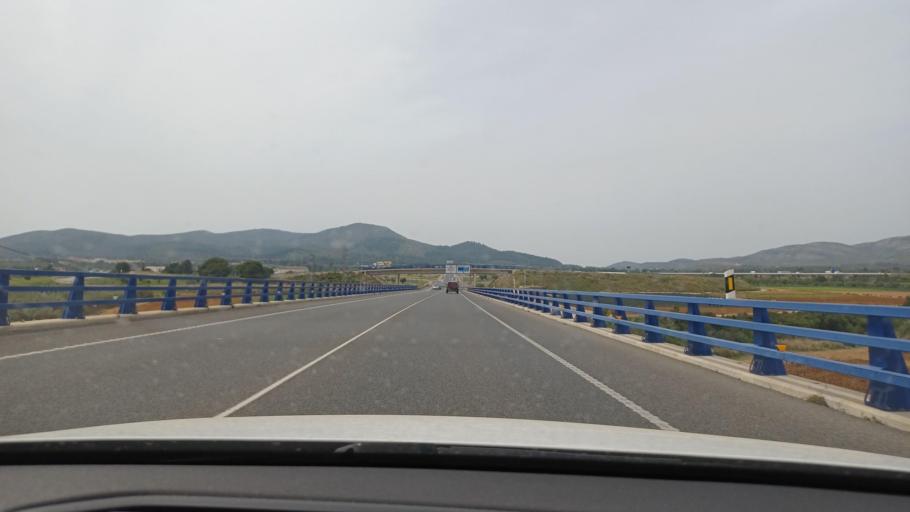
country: ES
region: Valencia
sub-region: Provincia de Castello
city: Benicarlo
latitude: 40.4085
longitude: 0.3797
